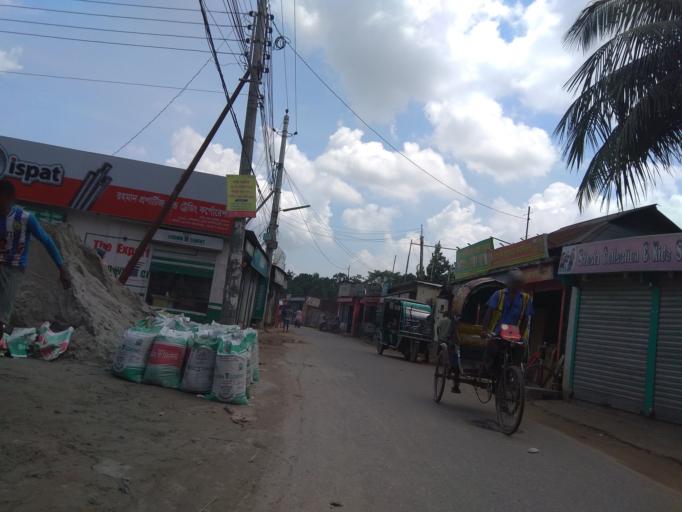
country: BD
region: Dhaka
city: Tungi
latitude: 23.8327
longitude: 90.3888
